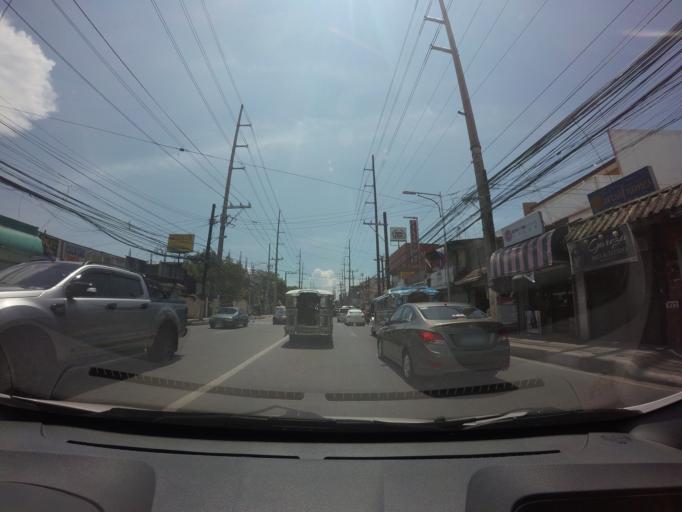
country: PH
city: Sambayanihan People's Village
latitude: 14.4369
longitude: 121.0076
